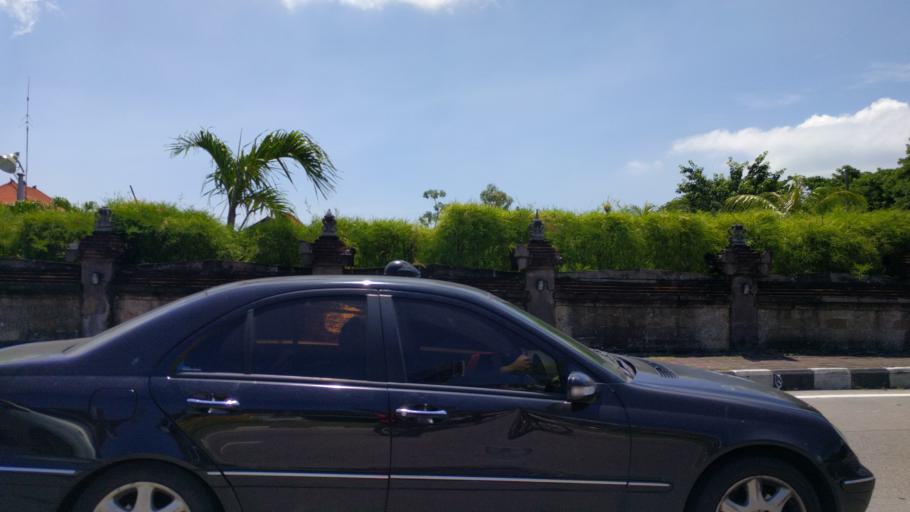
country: ID
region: Bali
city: Jabajero
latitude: -8.7246
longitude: 115.1812
